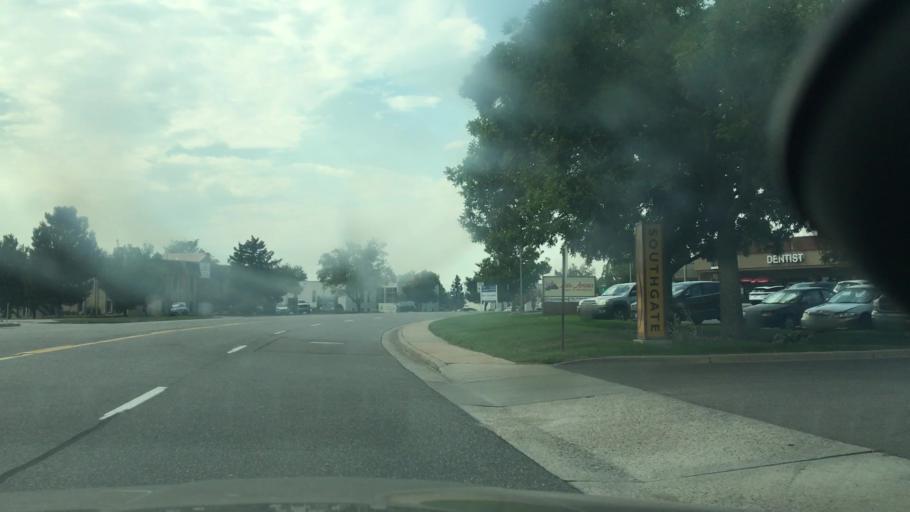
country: US
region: Colorado
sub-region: Arapahoe County
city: Castlewood
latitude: 39.5919
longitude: -104.8867
